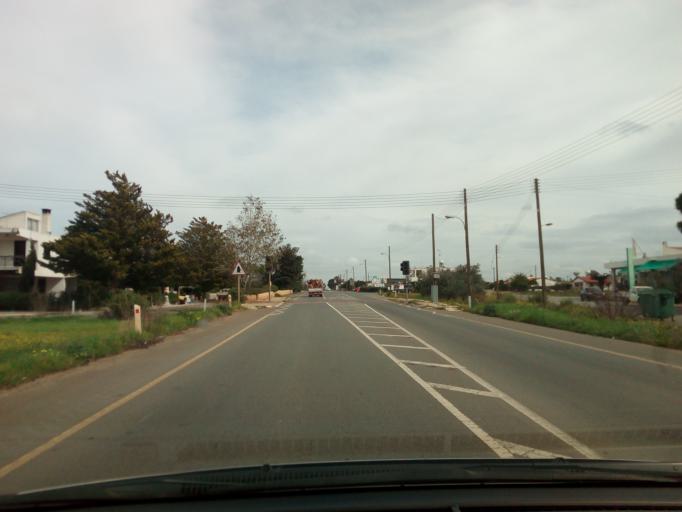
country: CY
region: Lefkosia
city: Peristerona
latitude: 35.1326
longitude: 33.0711
